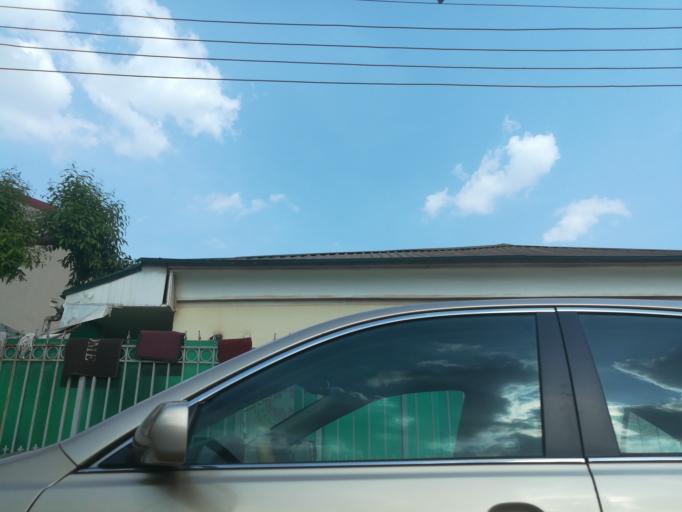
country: NG
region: Abuja Federal Capital Territory
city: Abuja
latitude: 9.0785
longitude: 7.4144
